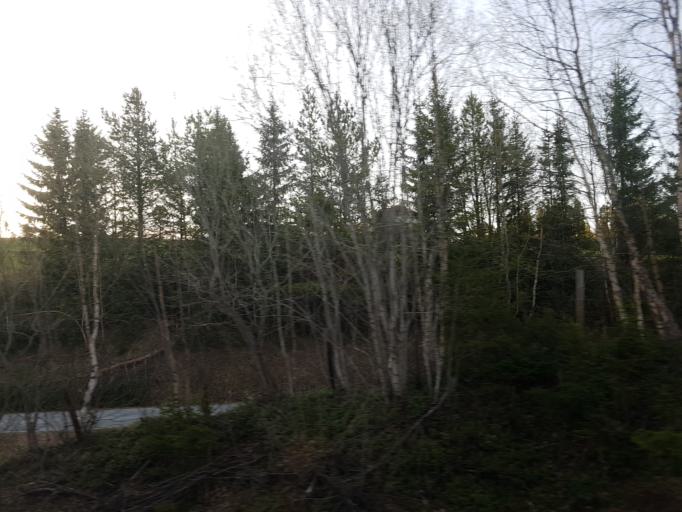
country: NO
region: Sor-Trondelag
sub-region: Rennebu
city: Berkak
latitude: 62.7462
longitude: 9.9841
